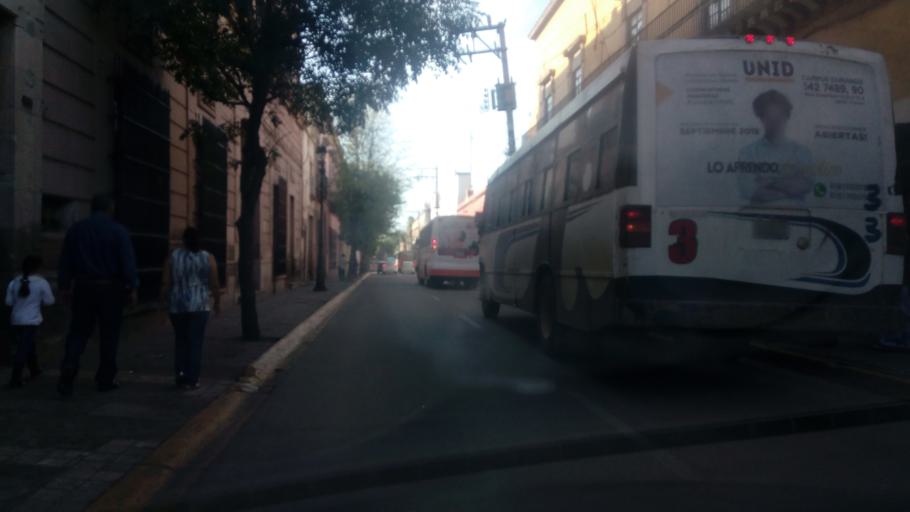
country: MX
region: Durango
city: Victoria de Durango
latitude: 24.0245
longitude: -104.6692
